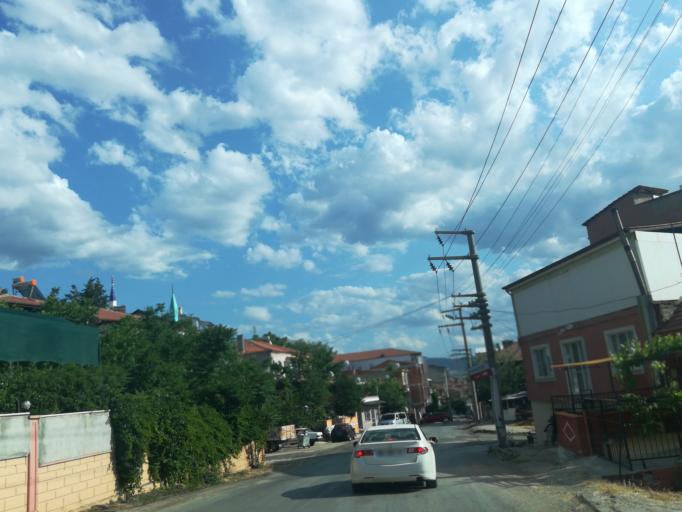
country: TR
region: Afyonkarahisar
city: Dinar
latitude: 38.0707
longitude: 30.1684
